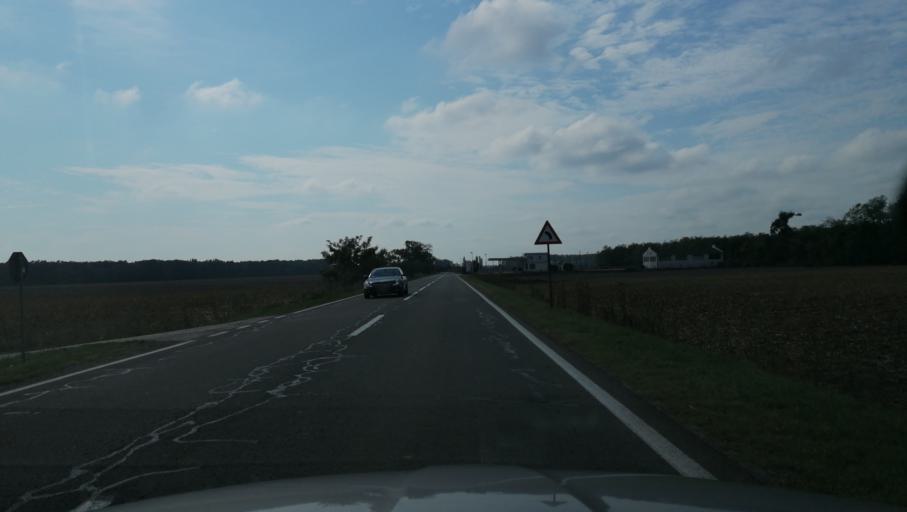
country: RS
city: Bosut
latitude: 44.9545
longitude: 19.3754
